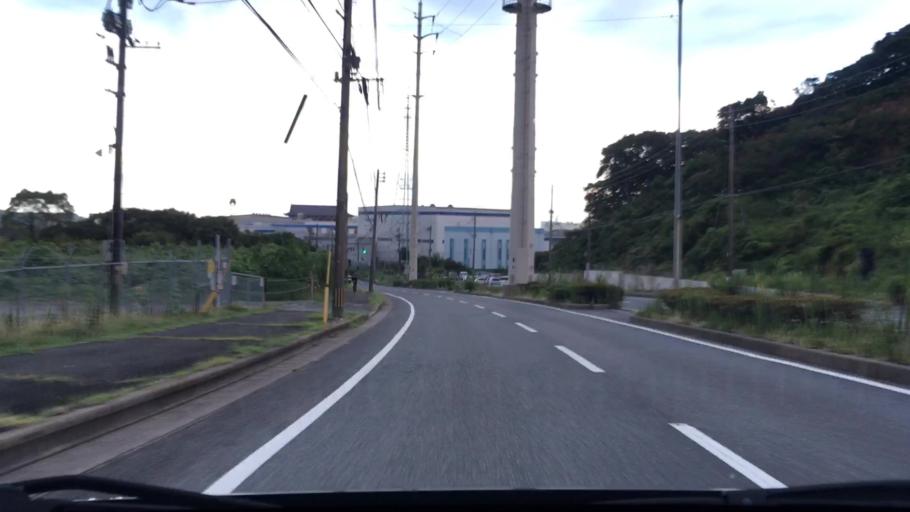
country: JP
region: Yamaguchi
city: Shimonoseki
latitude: 33.8868
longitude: 130.9825
